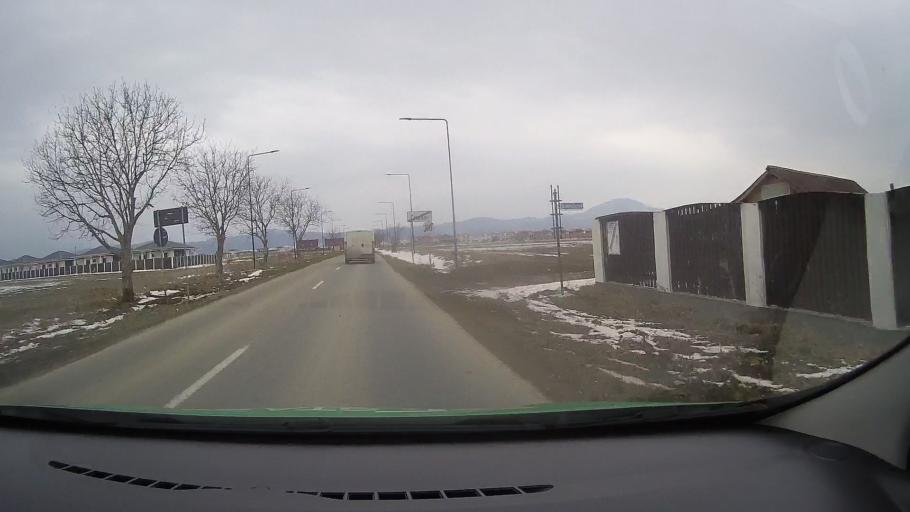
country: RO
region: Brasov
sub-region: Comuna Cristian
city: Cristian
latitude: 45.6279
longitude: 25.4697
